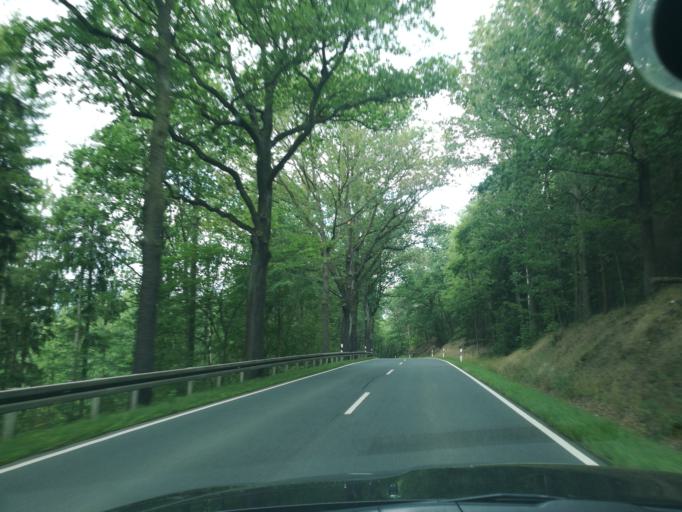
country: DE
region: Saxony
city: Oelsnitz
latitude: 50.3873
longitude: 12.1942
